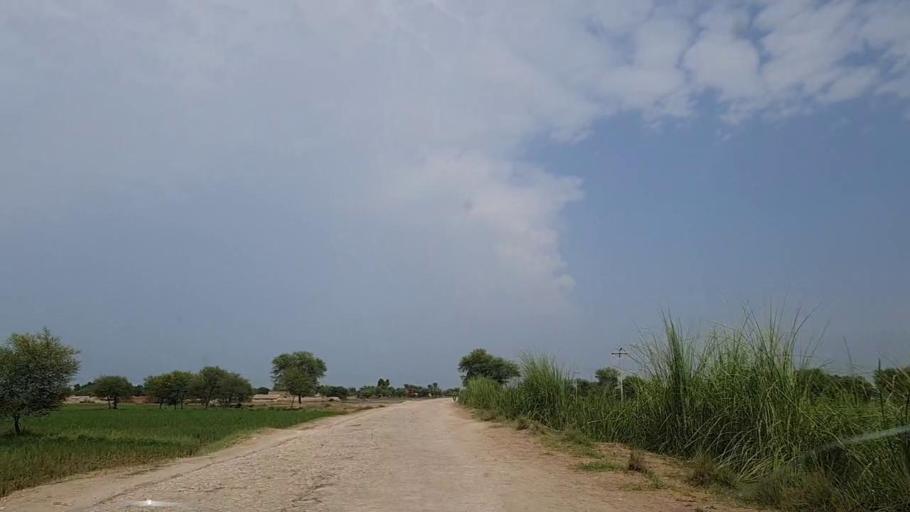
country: PK
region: Sindh
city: Khanpur
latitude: 27.8487
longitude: 69.4384
